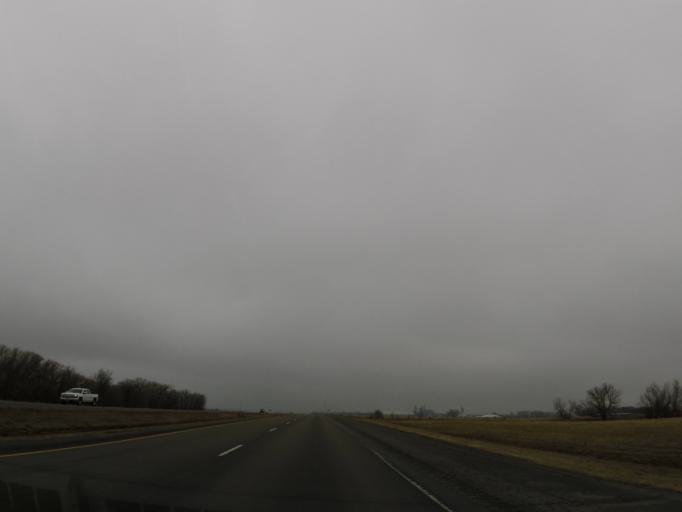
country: US
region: North Dakota
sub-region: Walsh County
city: Grafton
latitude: 48.5342
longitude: -97.1857
